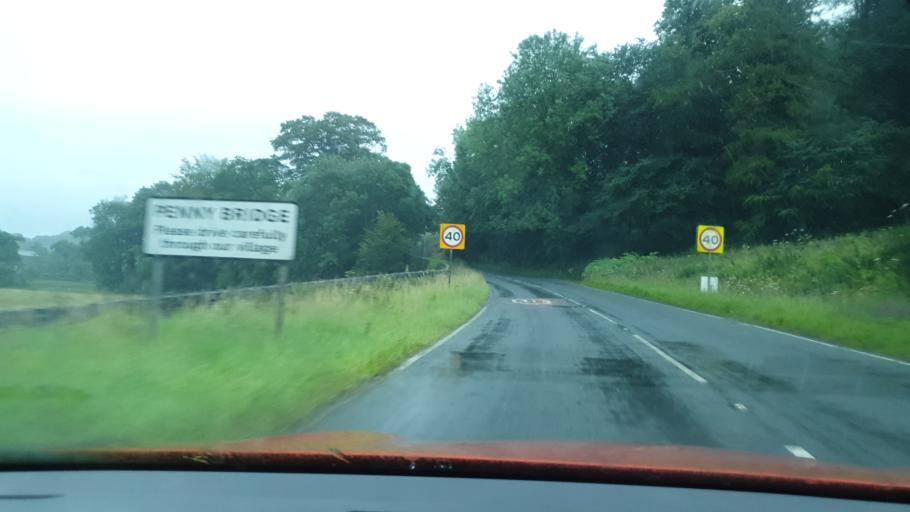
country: GB
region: England
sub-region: Cumbria
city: Ulverston
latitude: 54.2422
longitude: -3.0642
